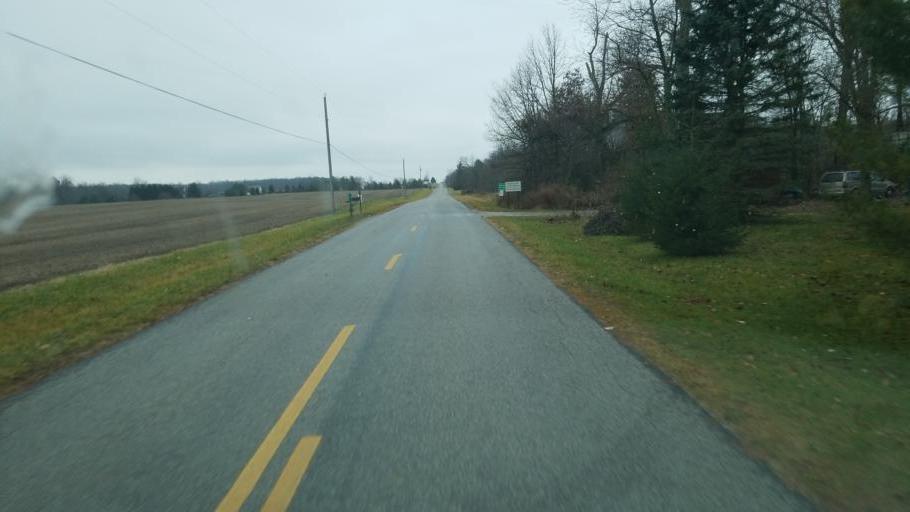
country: US
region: Ohio
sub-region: Delaware County
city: Ashley
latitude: 40.3627
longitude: -83.0204
